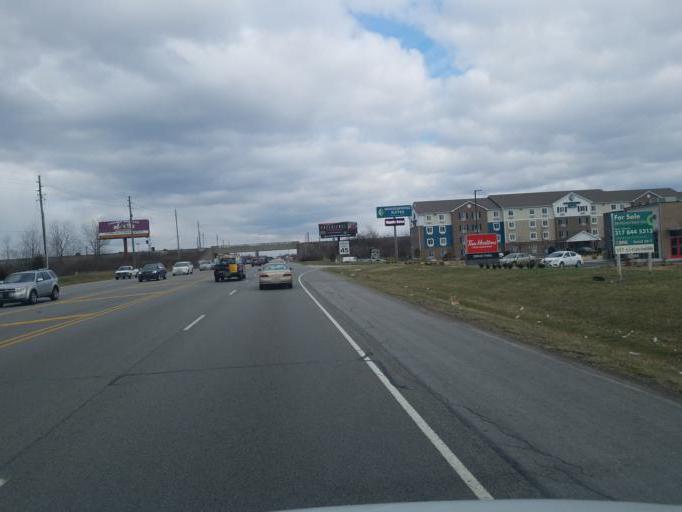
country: US
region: Indiana
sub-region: Marion County
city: Clermont
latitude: 39.7641
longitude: -86.3054
